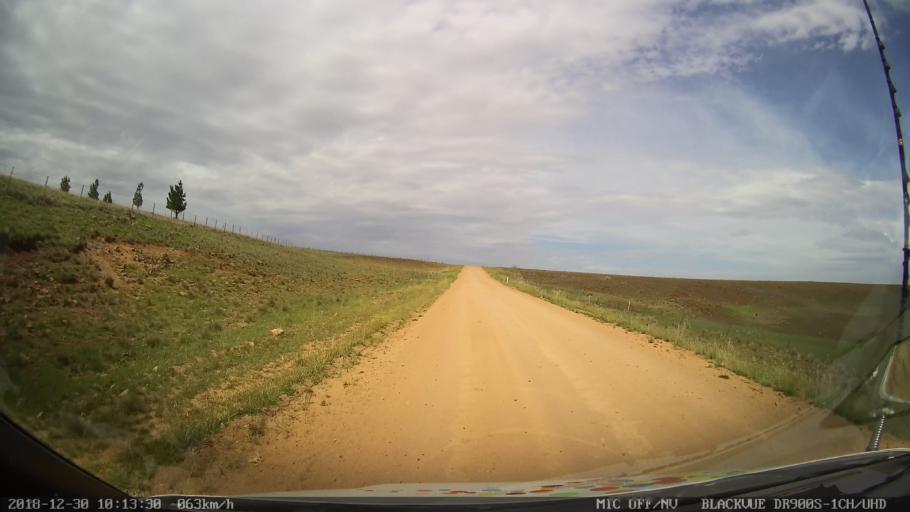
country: AU
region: New South Wales
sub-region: Snowy River
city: Berridale
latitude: -36.5383
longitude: 149.0644
